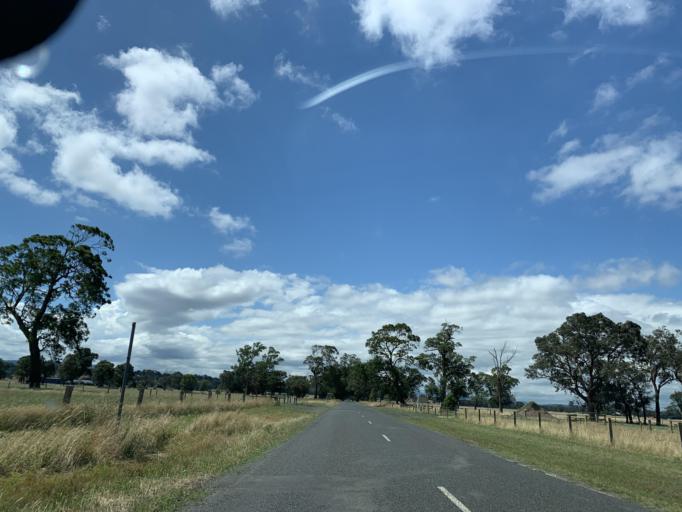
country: AU
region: Victoria
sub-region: Wellington
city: Heyfield
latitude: -37.9810
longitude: 146.6946
